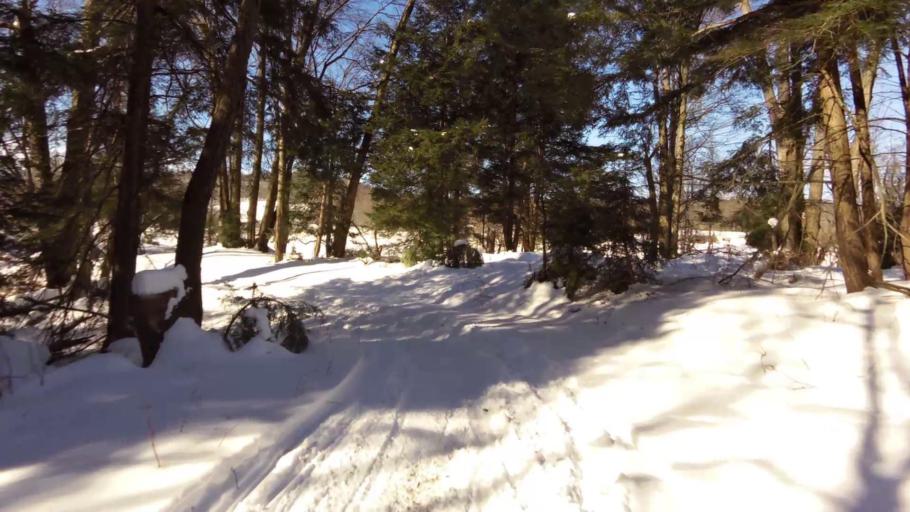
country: US
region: New York
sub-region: Allegany County
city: Cuba
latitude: 42.3483
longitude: -78.3068
